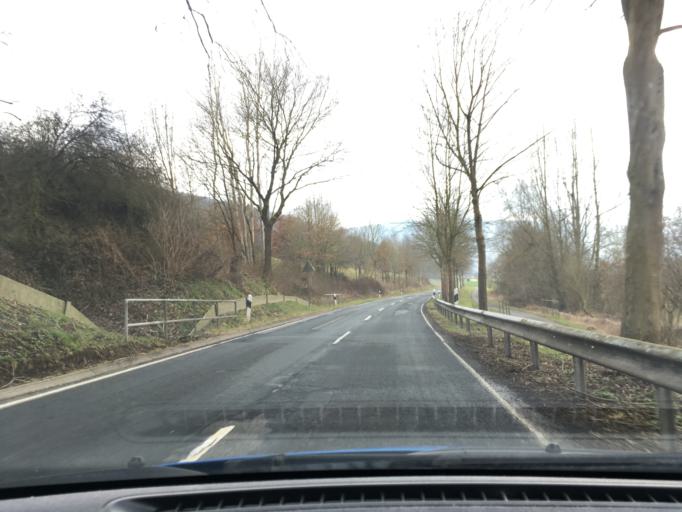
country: DE
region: Lower Saxony
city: Buhren
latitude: 51.5380
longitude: 9.6251
